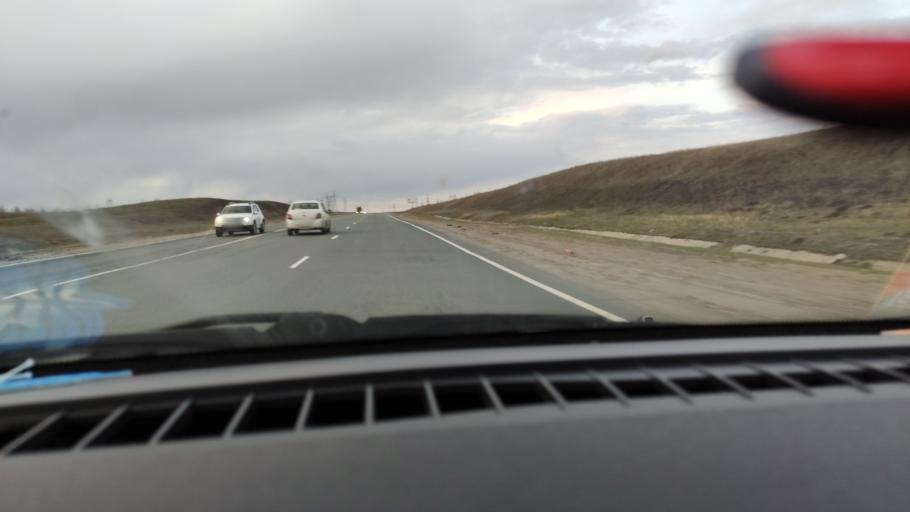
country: RU
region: Saratov
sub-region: Saratovskiy Rayon
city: Saratov
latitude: 51.7625
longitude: 46.0735
